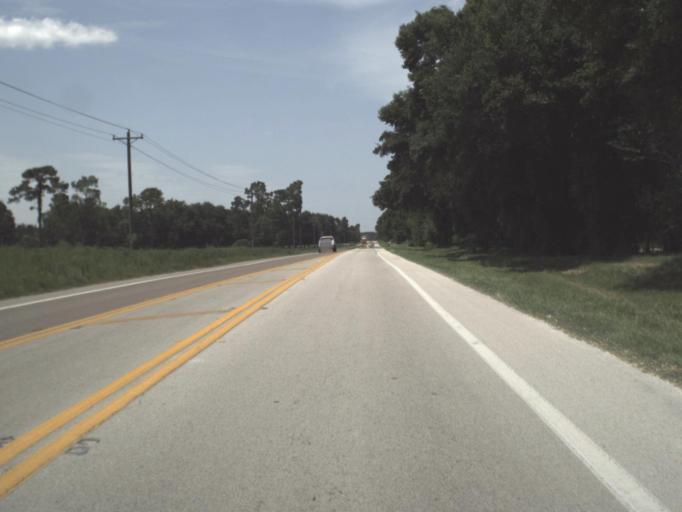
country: US
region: Florida
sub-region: Gilchrist County
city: Trenton
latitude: 29.7244
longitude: -82.8577
